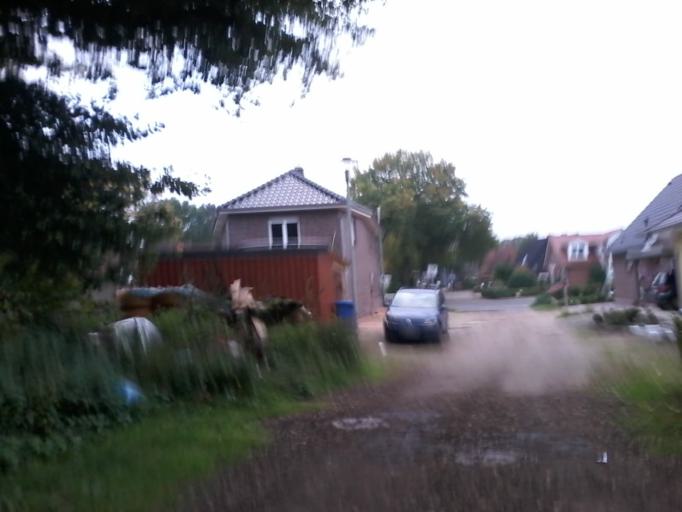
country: DE
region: Lower Saxony
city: Achim
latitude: 53.0009
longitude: 9.0650
